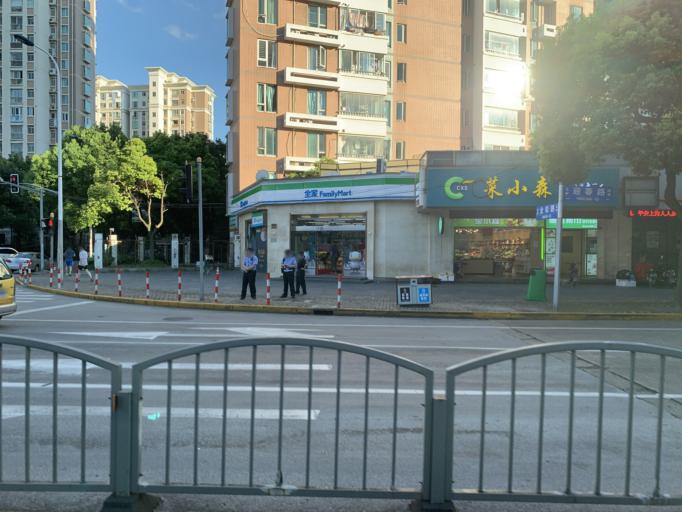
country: CN
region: Shanghai Shi
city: Huamu
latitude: 31.2260
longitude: 121.5504
